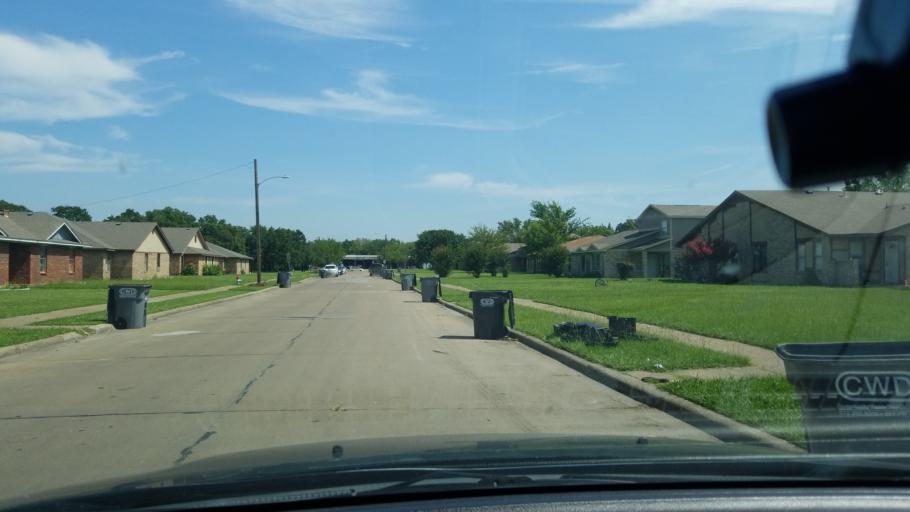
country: US
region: Texas
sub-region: Dallas County
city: Balch Springs
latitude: 32.7317
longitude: -96.6351
